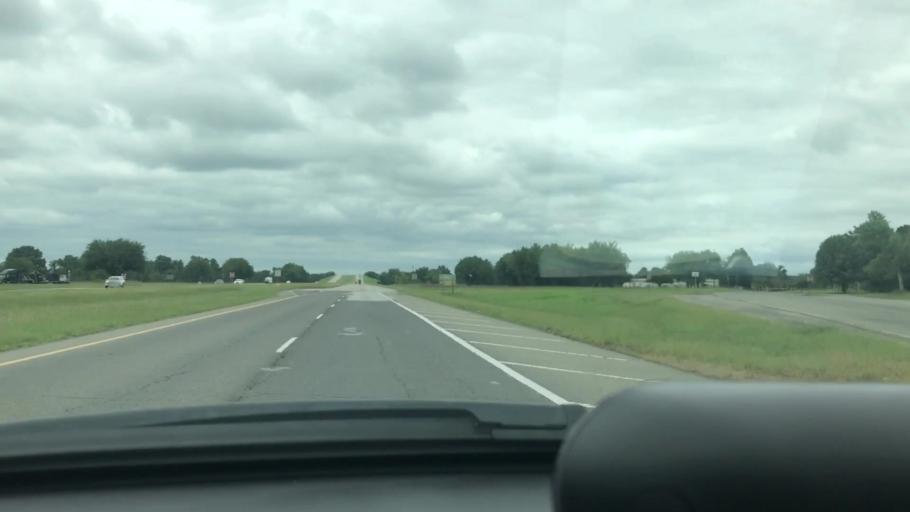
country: US
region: Oklahoma
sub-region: Wagoner County
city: Wagoner
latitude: 35.8697
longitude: -95.4025
